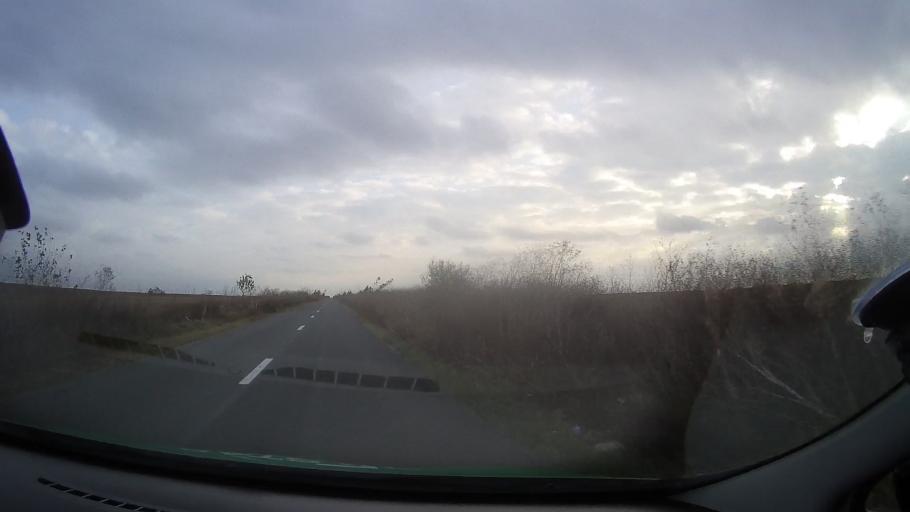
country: RO
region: Constanta
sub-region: Comuna Pestera
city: Pestera
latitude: 44.1441
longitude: 28.1160
